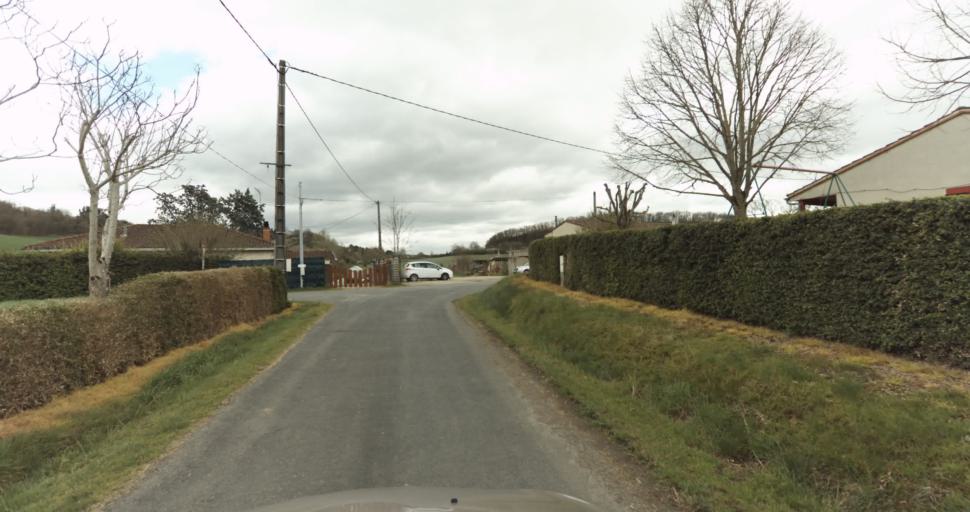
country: FR
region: Midi-Pyrenees
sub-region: Departement du Tarn
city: Puygouzon
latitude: 43.8711
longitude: 2.1813
